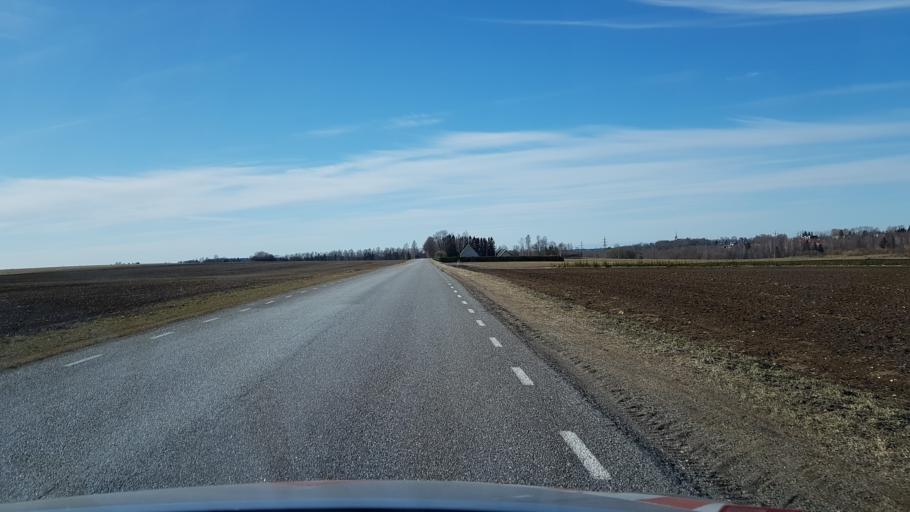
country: EE
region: Laeaene-Virumaa
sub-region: Kadrina vald
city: Kadrina
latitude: 59.3289
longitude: 26.1362
